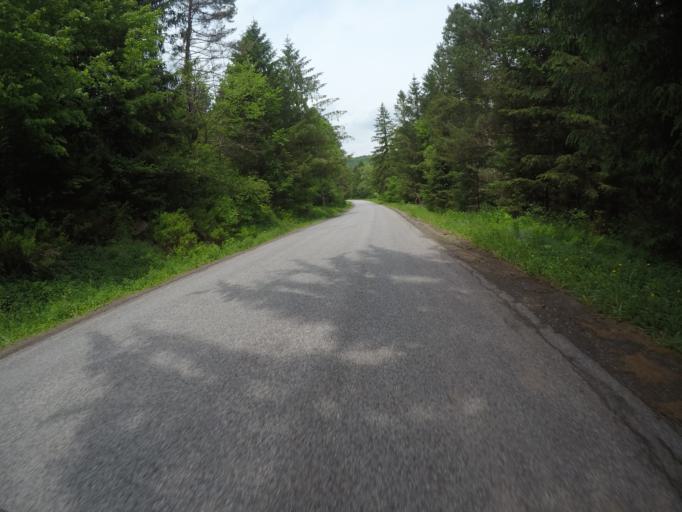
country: US
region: New York
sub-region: Delaware County
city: Stamford
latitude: 42.2644
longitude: -74.7245
